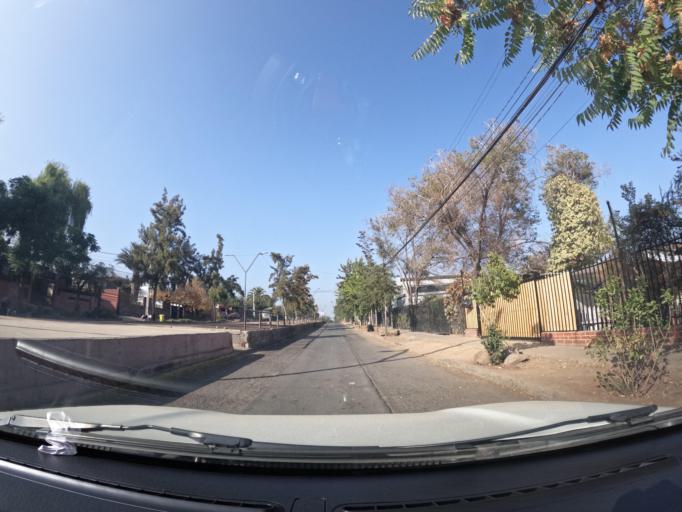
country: CL
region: Santiago Metropolitan
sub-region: Provincia de Santiago
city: Villa Presidente Frei, Nunoa, Santiago, Chile
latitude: -33.4718
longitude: -70.5313
